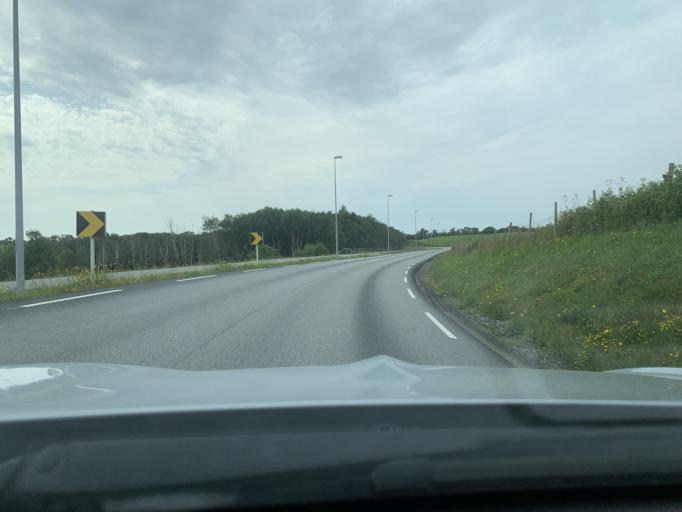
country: NO
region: Rogaland
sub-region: Time
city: Bryne
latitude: 58.7641
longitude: 5.7143
